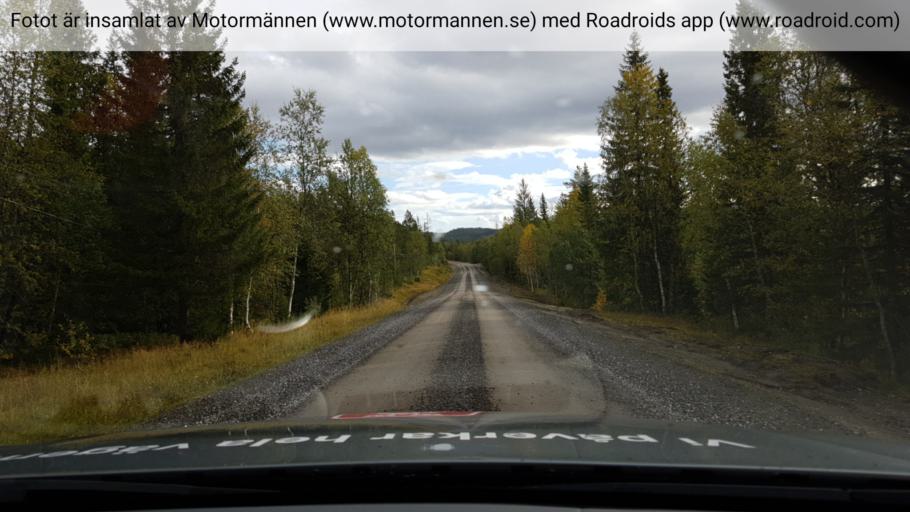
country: NO
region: Nord-Trondelag
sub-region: Snasa
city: Snaase
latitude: 63.7306
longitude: 12.5322
